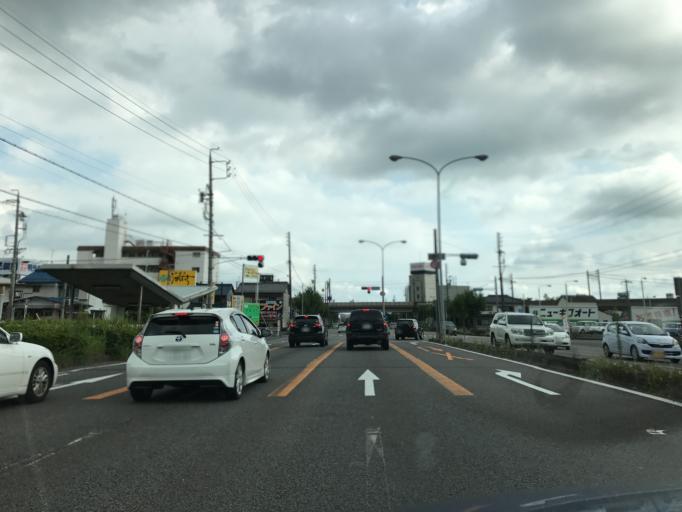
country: JP
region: Gifu
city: Gifu-shi
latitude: 35.4034
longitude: 136.7847
